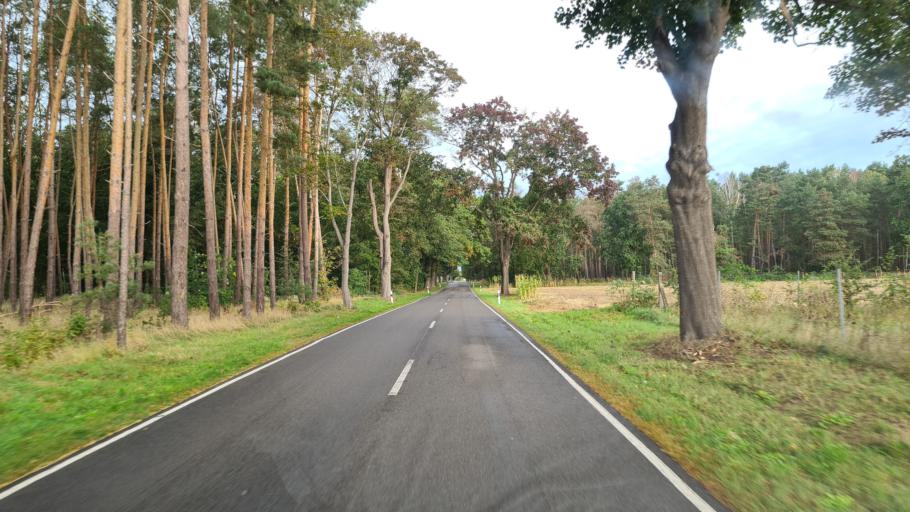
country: DE
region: Brandenburg
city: Kasel-Golzig
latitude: 51.9190
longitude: 13.7127
